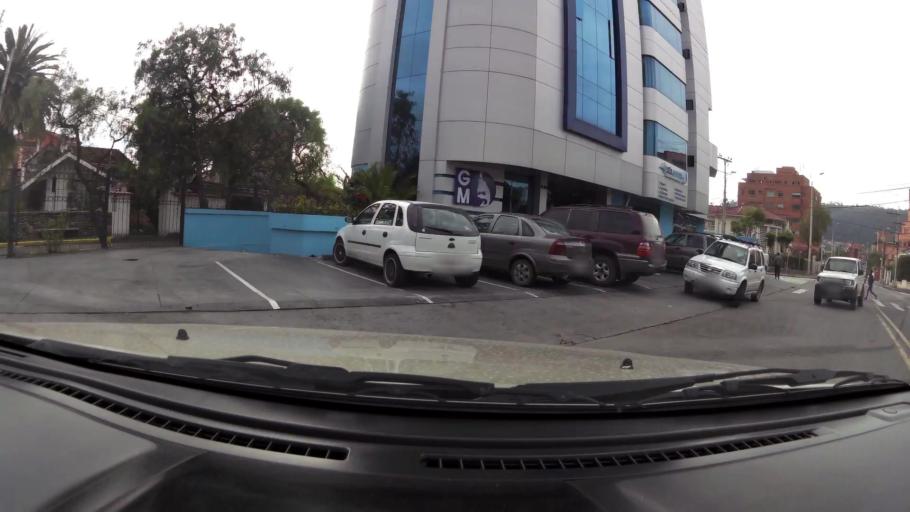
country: EC
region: Azuay
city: Cuenca
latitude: -2.9086
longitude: -78.9997
